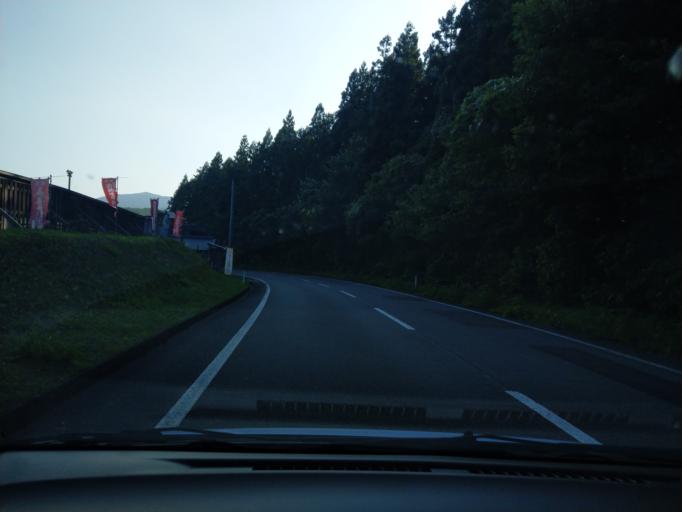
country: JP
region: Akita
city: Akita
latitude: 39.5758
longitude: 140.2330
